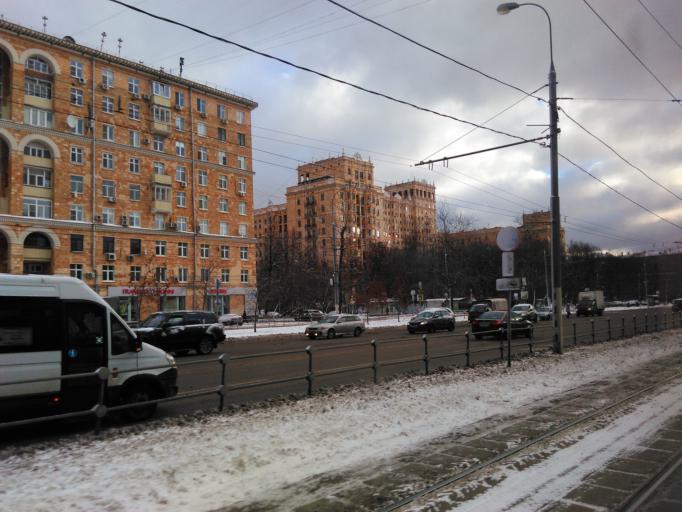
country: RU
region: Moskovskaya
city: Semenovskoye
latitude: 55.6916
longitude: 37.5388
